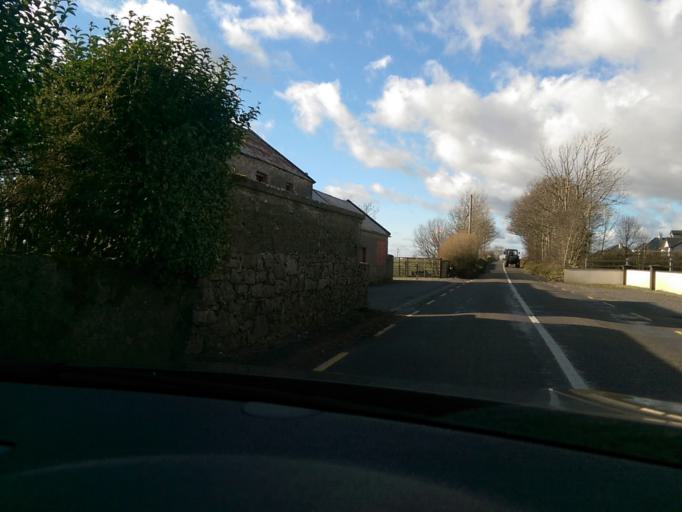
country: IE
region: Connaught
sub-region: Roscommon
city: Castlerea
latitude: 53.5846
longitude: -8.5641
